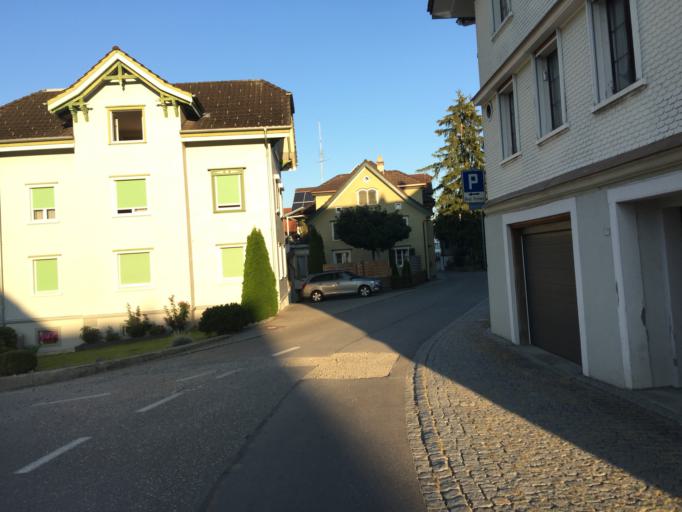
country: CH
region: Saint Gallen
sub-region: Wahlkreis Wil
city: Oberuzwil
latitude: 47.4205
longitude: 9.1368
